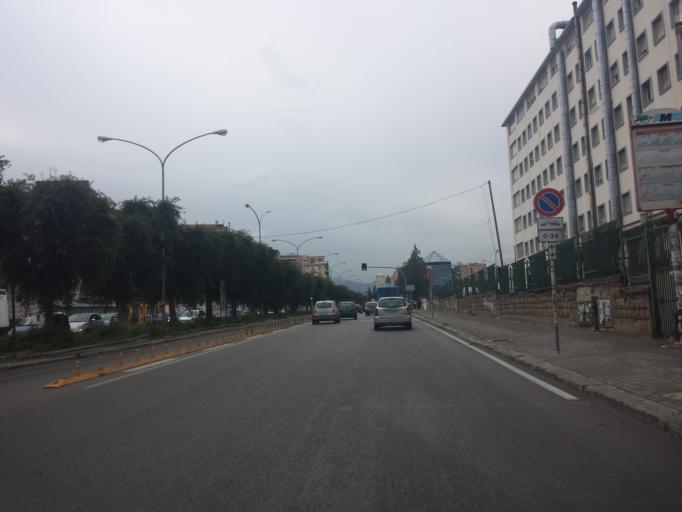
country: IT
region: Sicily
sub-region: Palermo
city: Palermo
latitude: 38.1066
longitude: 13.3527
